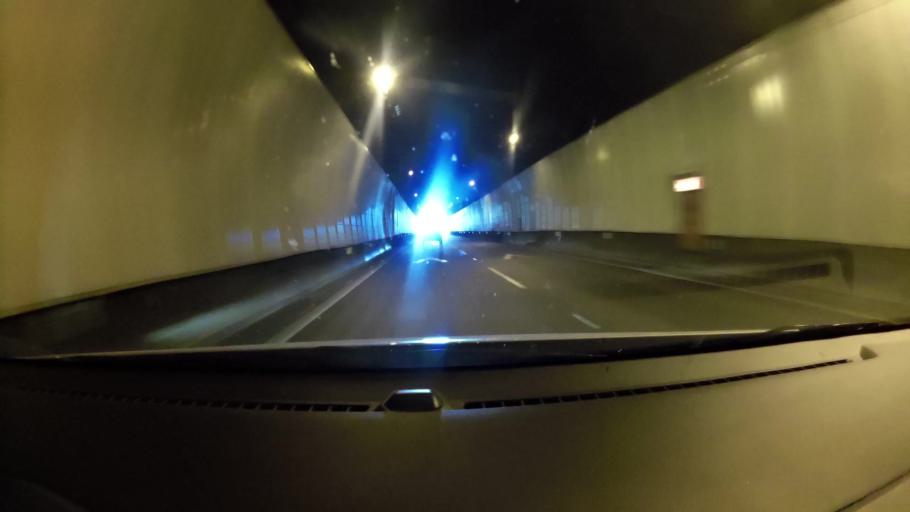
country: CL
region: Santiago Metropolitan
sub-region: Provincia de Melipilla
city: Melipilla
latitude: -33.3851
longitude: -71.2715
